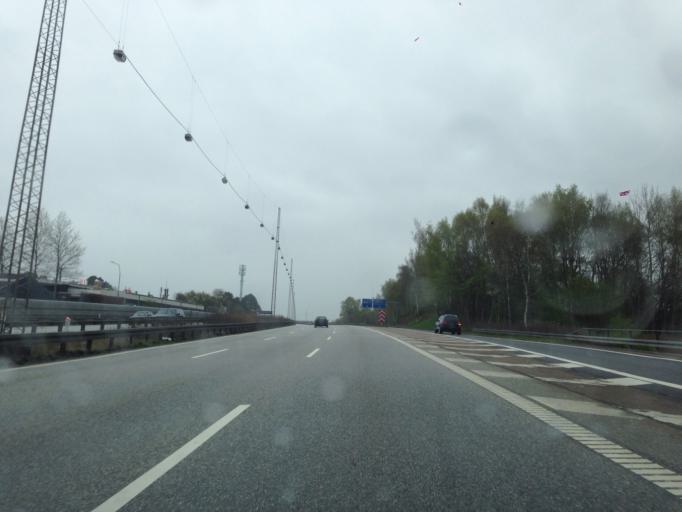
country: DK
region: Capital Region
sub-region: Rudersdal Kommune
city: Trorod
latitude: 55.8192
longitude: 12.5263
